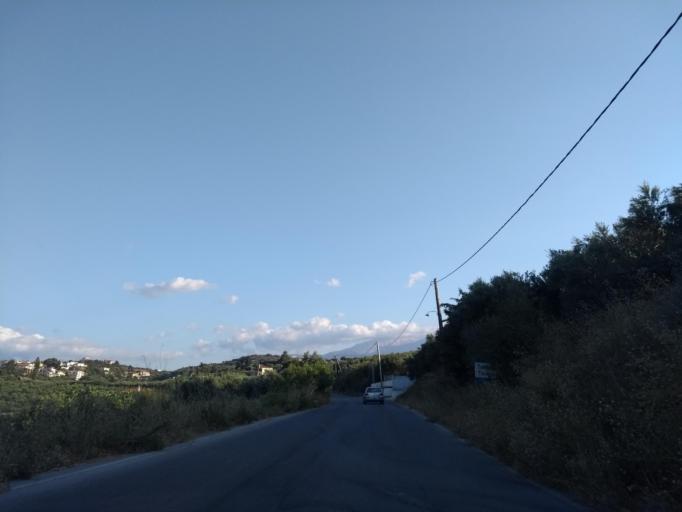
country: GR
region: Crete
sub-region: Nomos Chanias
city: Kalivai
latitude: 35.4423
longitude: 24.1757
